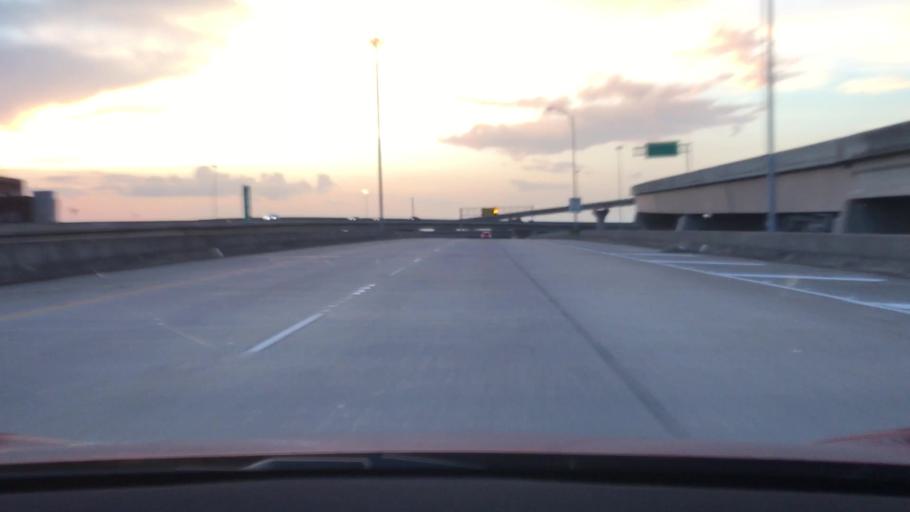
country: US
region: Louisiana
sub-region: Caddo Parish
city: Shreveport
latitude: 32.4935
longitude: -93.7572
